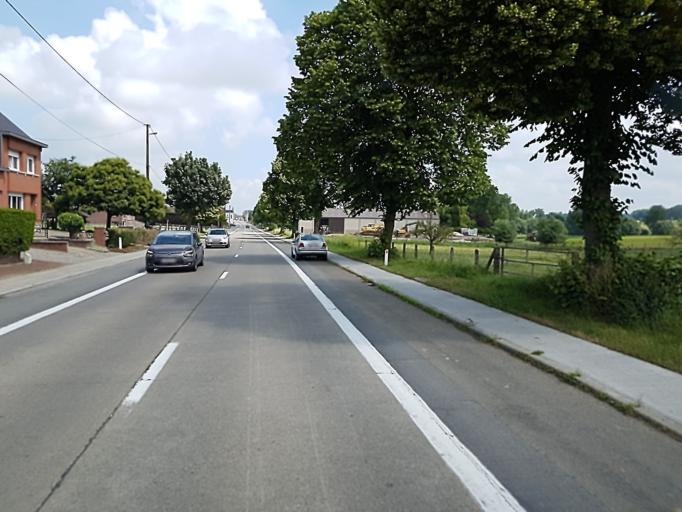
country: BE
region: Flanders
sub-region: Provincie Vlaams-Brabant
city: Gooik
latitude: 50.7394
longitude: 4.0936
